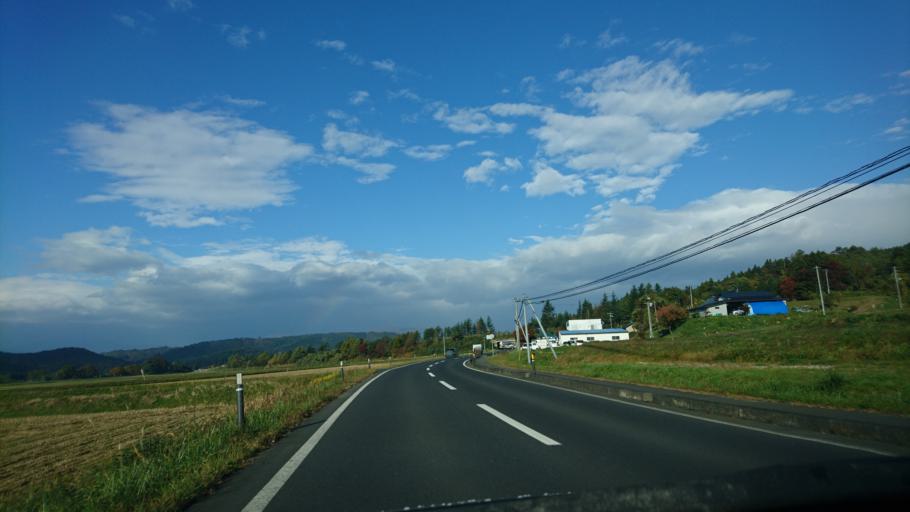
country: JP
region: Iwate
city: Ichinoseki
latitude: 39.0155
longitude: 141.1040
